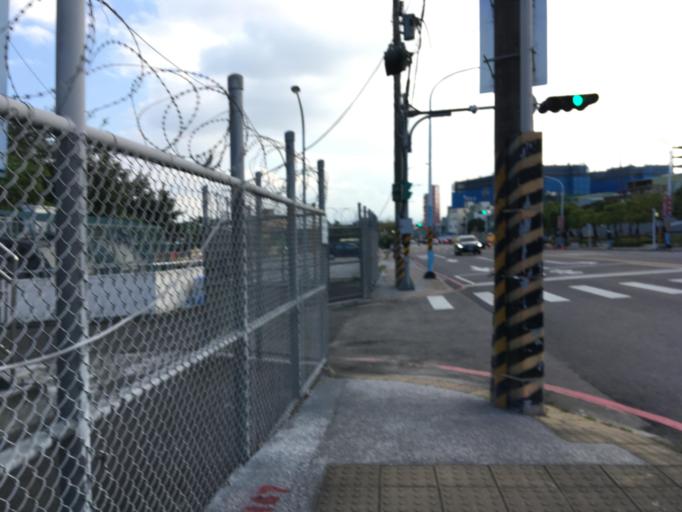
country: TW
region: Taipei
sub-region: Taipei
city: Banqiao
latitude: 25.0277
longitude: 121.4350
